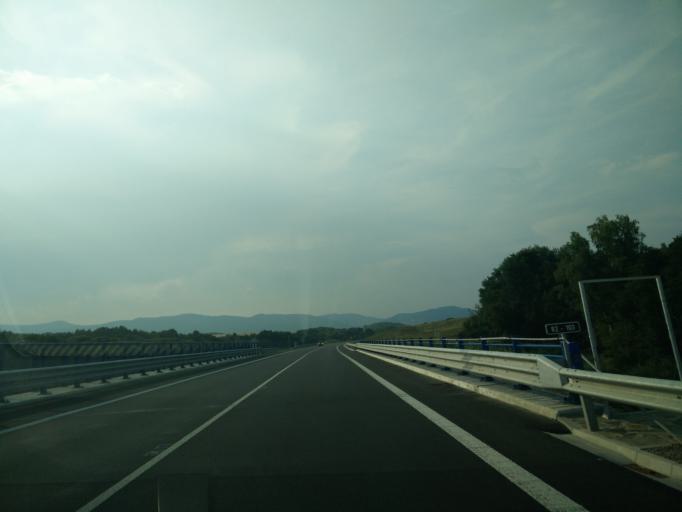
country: SK
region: Banskobystricky
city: Ziar nad Hronom
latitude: 48.5918
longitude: 18.8280
